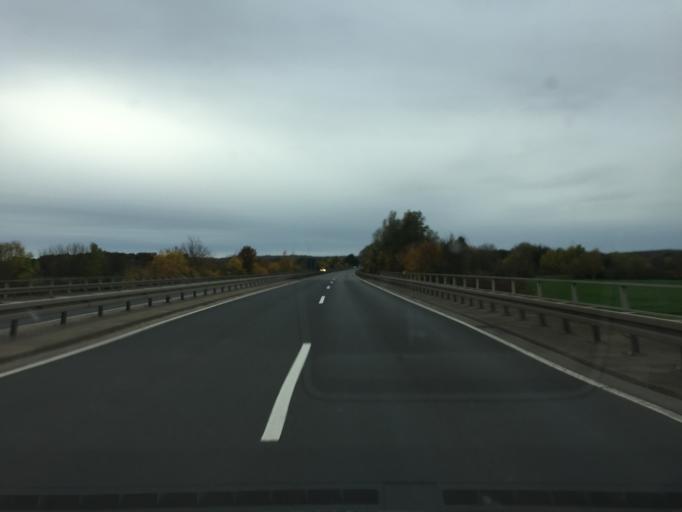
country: DE
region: Lower Saxony
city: Marklohe
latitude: 52.6545
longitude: 9.1798
